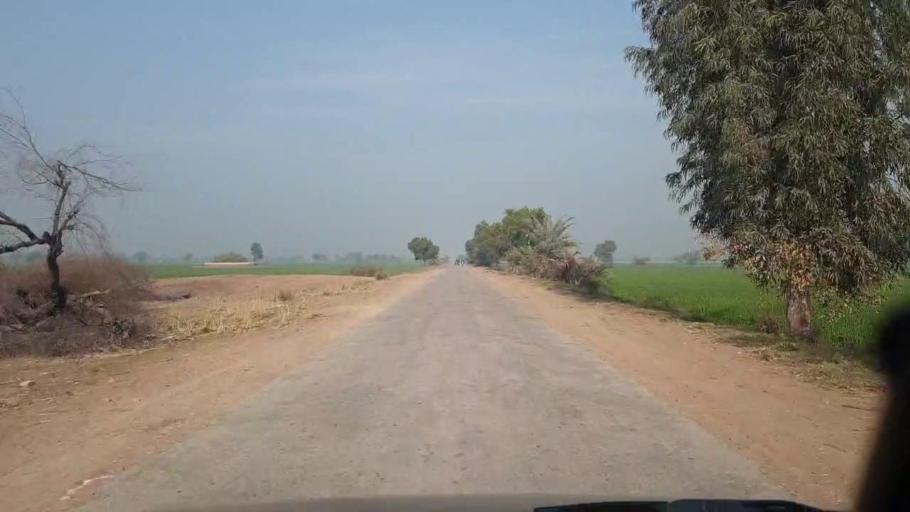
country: PK
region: Sindh
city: Shahdadpur
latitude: 25.9803
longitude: 68.5720
